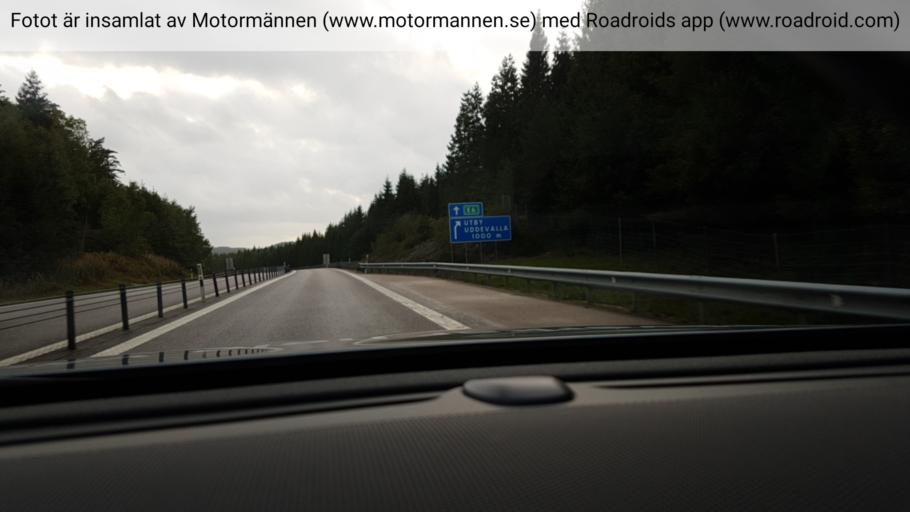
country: SE
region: Vaestra Goetaland
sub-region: Uddevalla Kommun
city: Uddevalla
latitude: 58.3245
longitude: 11.9588
